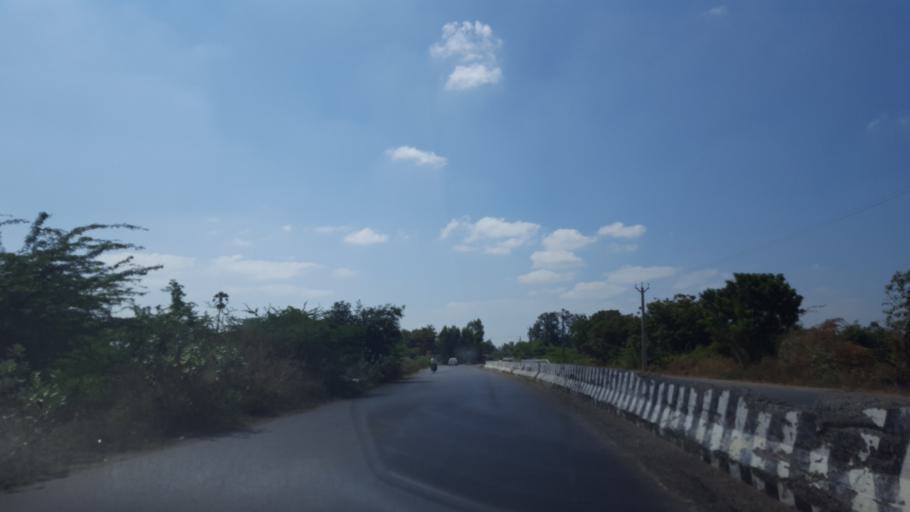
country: IN
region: Tamil Nadu
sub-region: Kancheepuram
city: Mamallapuram
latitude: 12.7043
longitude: 80.1836
